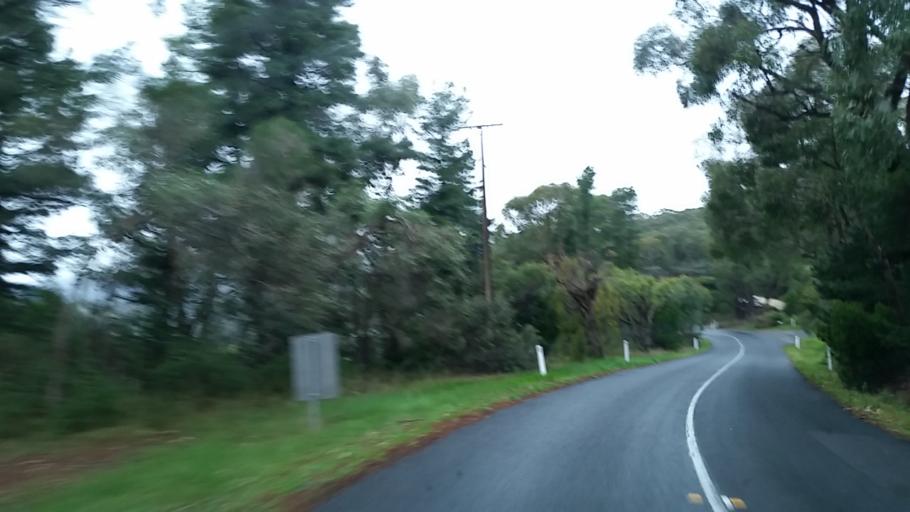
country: AU
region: South Australia
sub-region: Adelaide Hills
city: Bridgewater
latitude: -34.9519
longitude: 138.7596
